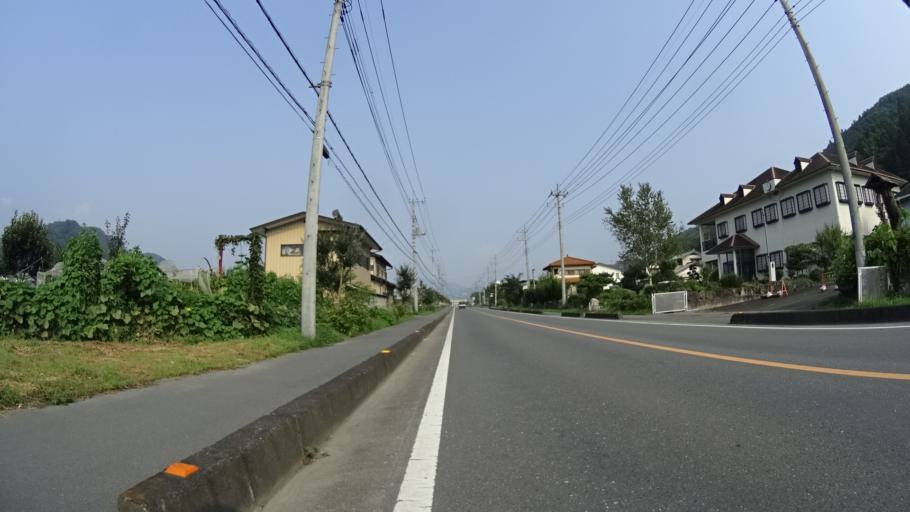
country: JP
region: Saitama
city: Chichibu
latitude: 36.0161
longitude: 139.0178
